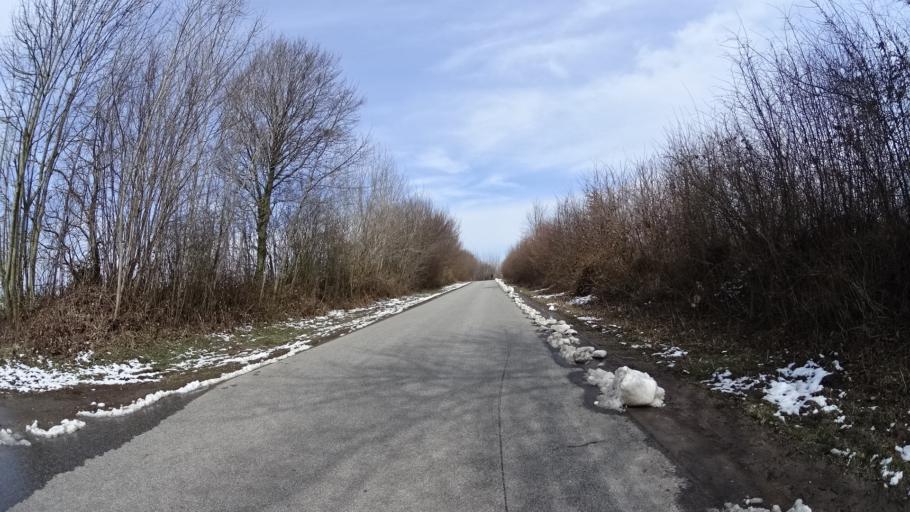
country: DE
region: Schleswig-Holstein
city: Stolpe
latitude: 54.1324
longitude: 10.2195
